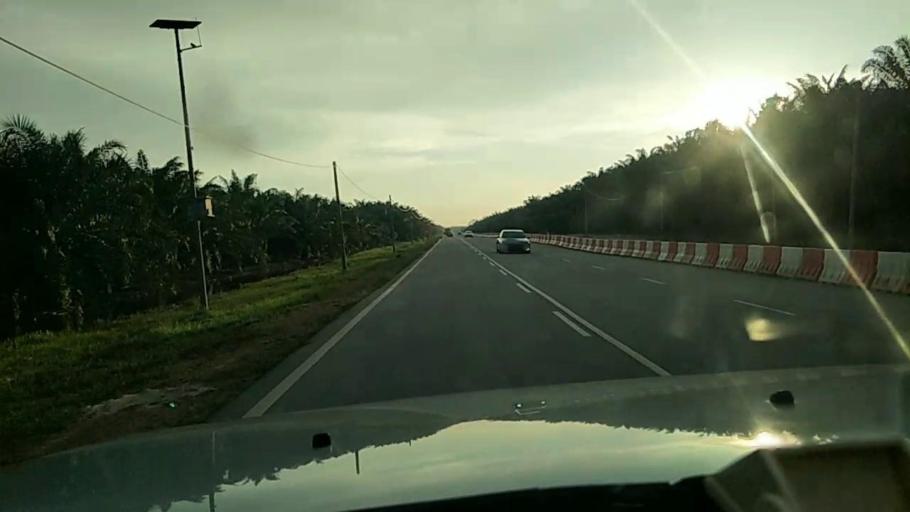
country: MY
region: Selangor
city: Batang Berjuntai
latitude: 3.3070
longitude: 101.3679
